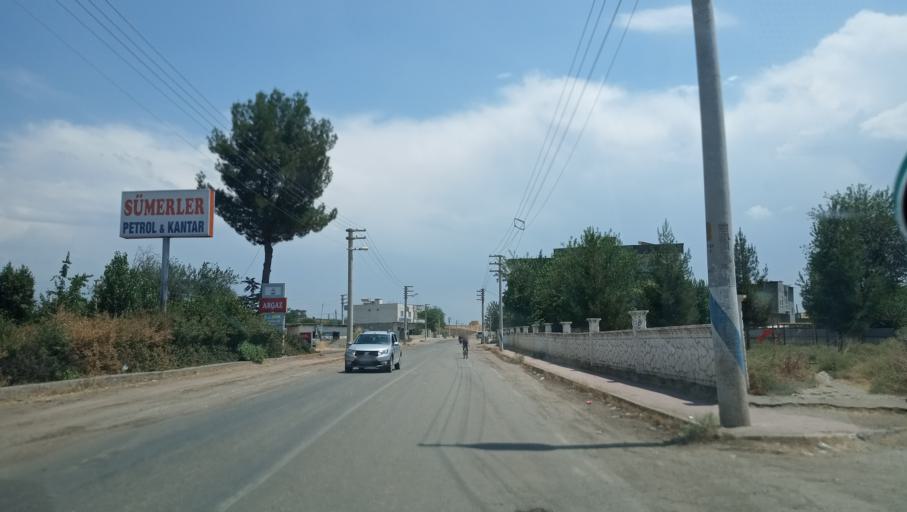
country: TR
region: Diyarbakir
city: Tepe
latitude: 37.7928
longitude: 40.7781
